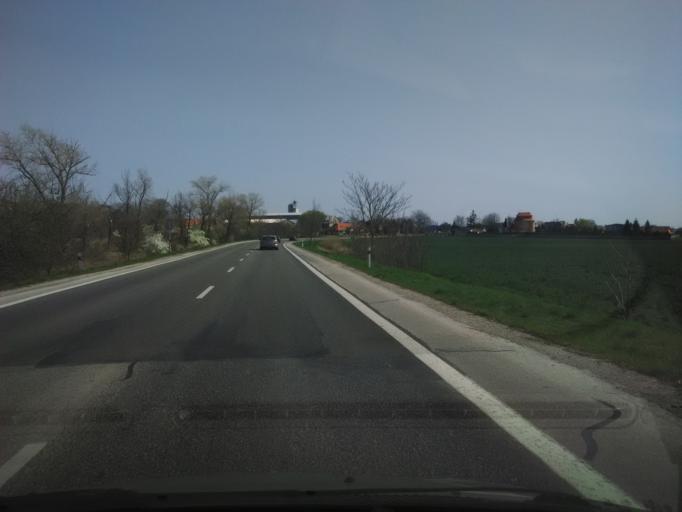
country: SK
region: Nitriansky
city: Sellye
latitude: 48.1353
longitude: 18.0189
